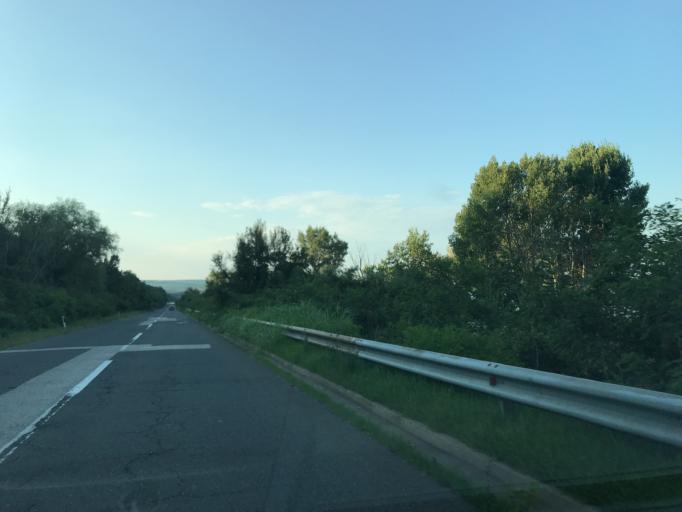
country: RO
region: Mehedinti
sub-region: Comuna Gogosu
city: Ostrovu Mare
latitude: 44.4542
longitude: 22.4526
